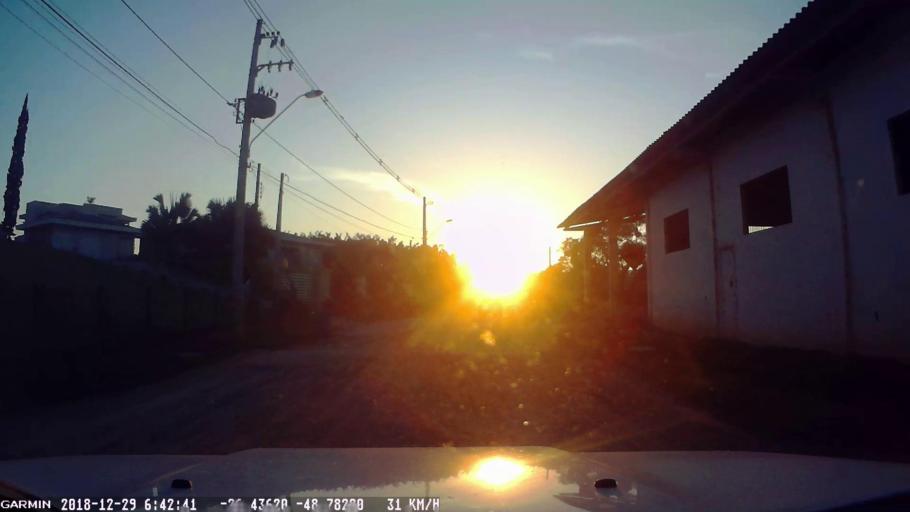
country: BR
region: Santa Catarina
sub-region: Joinville
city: Joinville
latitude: -26.4362
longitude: -48.7825
